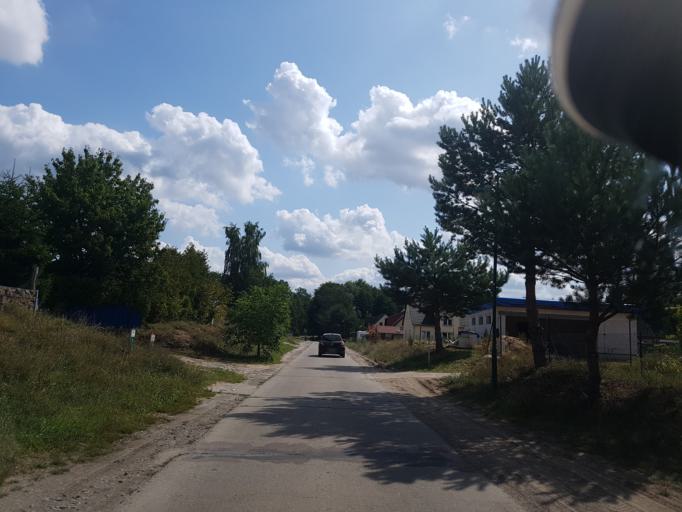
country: DE
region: Brandenburg
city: Gross Kreutz
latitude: 52.3180
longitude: 12.7679
